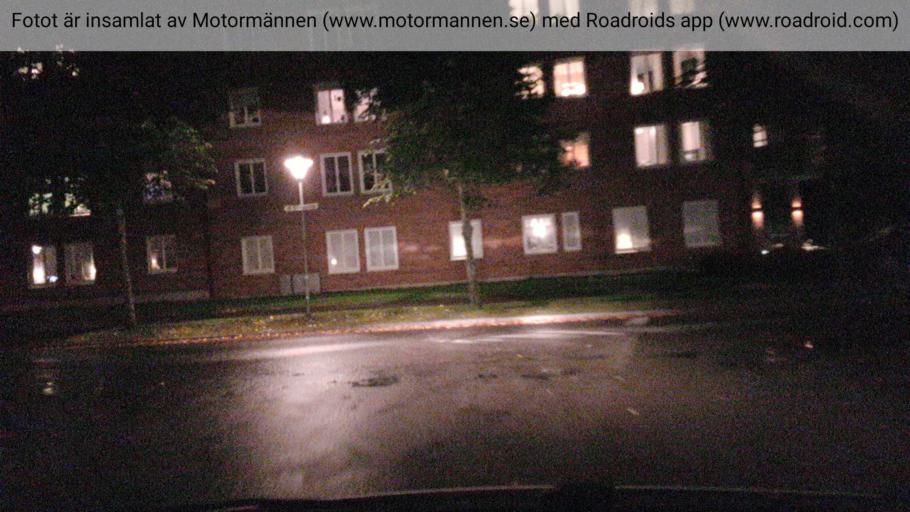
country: SE
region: Vaestra Goetaland
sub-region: Skovde Kommun
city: Skoevde
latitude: 58.3976
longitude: 13.8578
